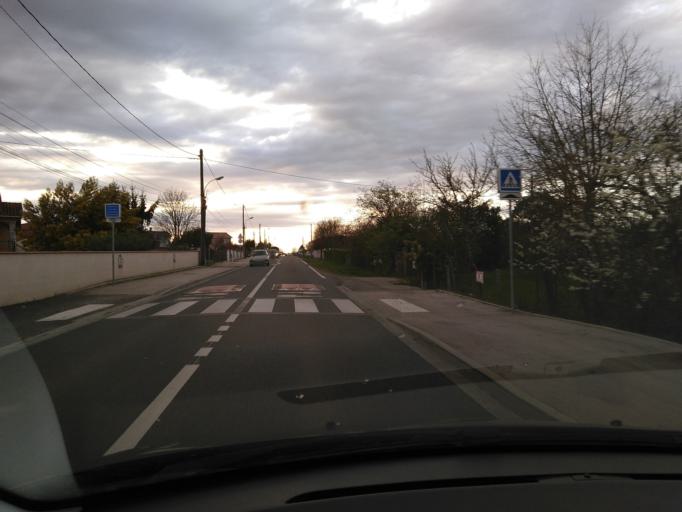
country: FR
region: Midi-Pyrenees
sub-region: Departement de la Haute-Garonne
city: Pibrac
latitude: 43.6060
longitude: 1.2733
